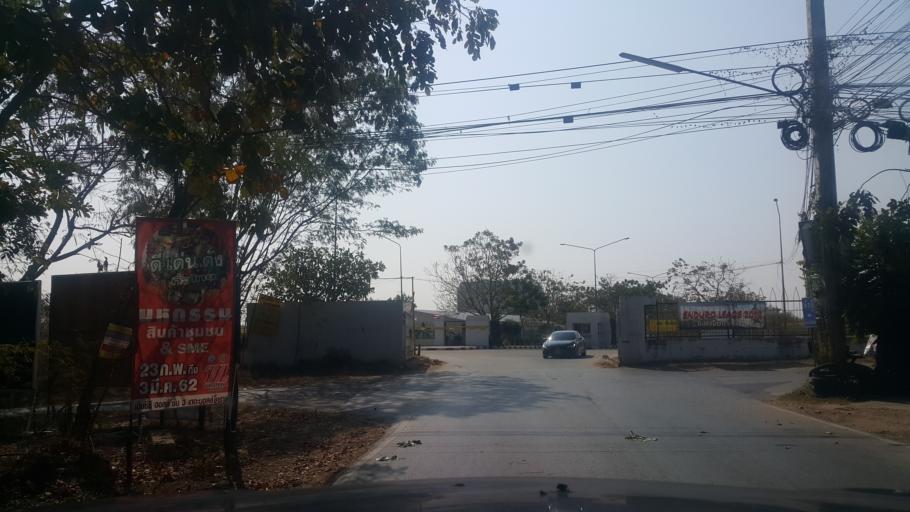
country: TH
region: Nakhon Ratchasima
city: Nakhon Ratchasima
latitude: 14.9312
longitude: 102.0441
